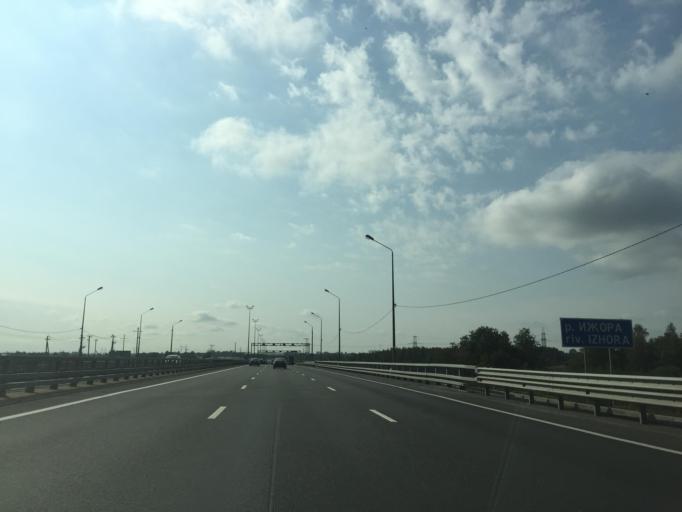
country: RU
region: Leningrad
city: Maloye Verevo
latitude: 59.6070
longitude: 30.1865
